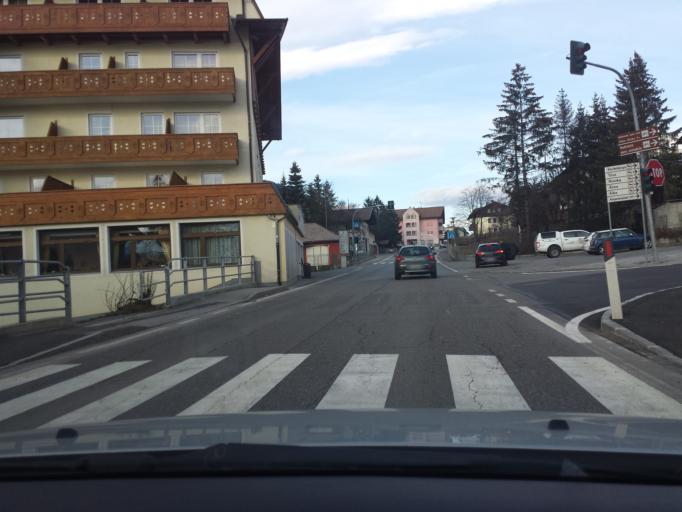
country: IT
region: Trentino-Alto Adige
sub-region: Bolzano
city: Curon Venosta
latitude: 46.7636
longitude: 10.5338
